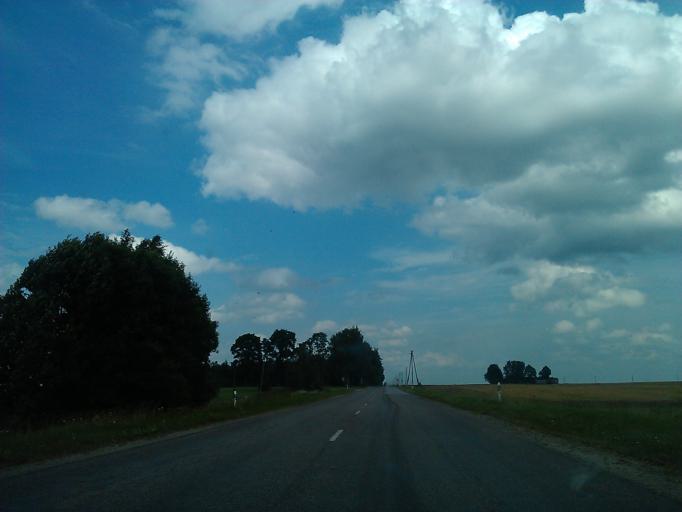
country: LV
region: Burtnieki
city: Matisi
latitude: 57.7119
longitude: 25.1588
